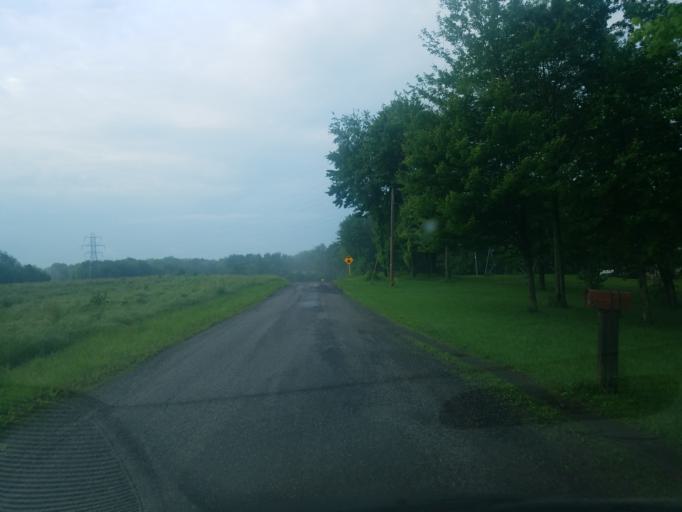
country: US
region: Ohio
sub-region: Stark County
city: Minerva
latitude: 40.7558
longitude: -80.9628
